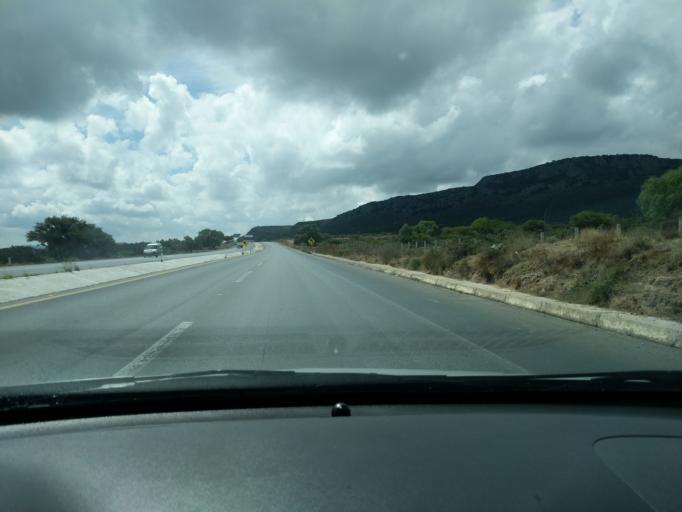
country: MX
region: Zacatecas
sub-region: Pinos
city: Santiago
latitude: 22.4035
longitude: -101.3846
